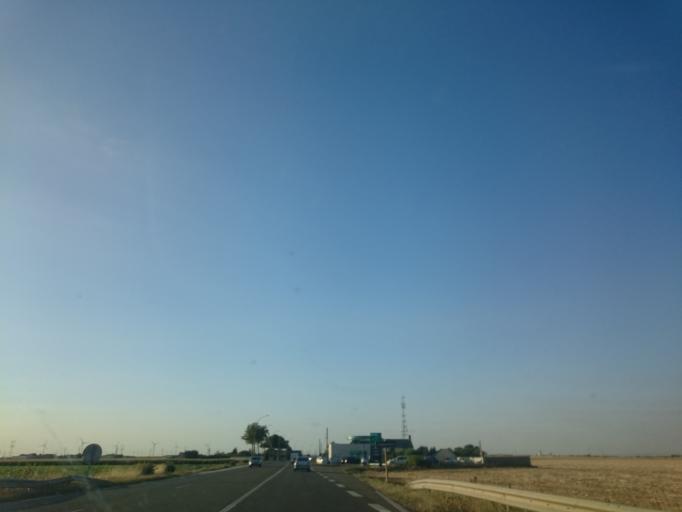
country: FR
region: Centre
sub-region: Departement d'Eure-et-Loir
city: Toury
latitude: 48.2238
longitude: 1.9511
